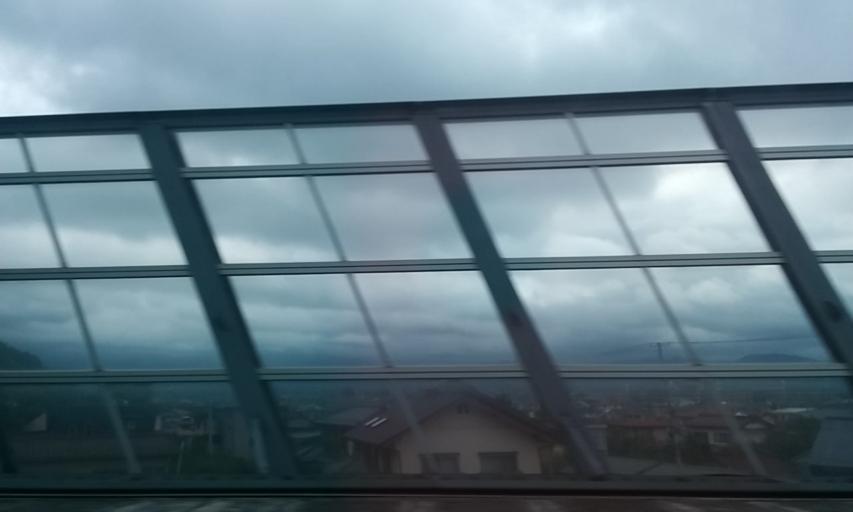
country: JP
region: Fukushima
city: Fukushima-shi
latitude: 37.7739
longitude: 140.4621
